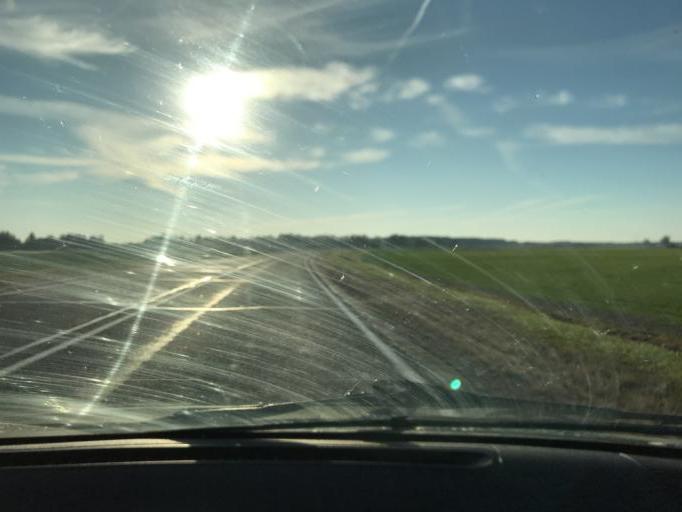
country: BY
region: Brest
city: Horad Kobryn
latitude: 52.2111
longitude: 24.4805
